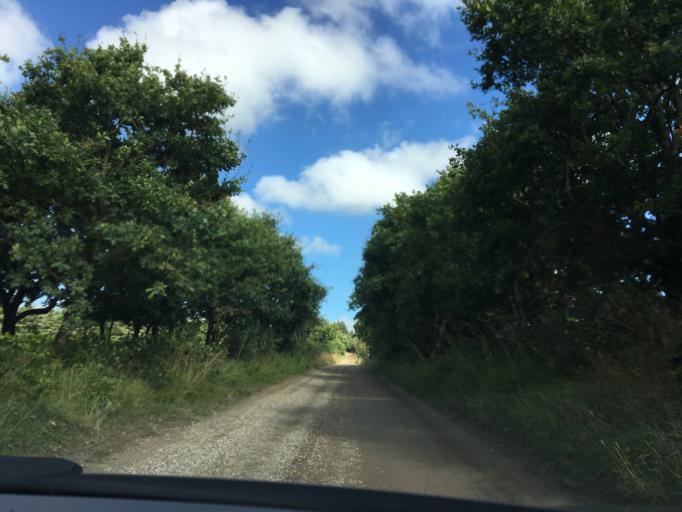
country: DK
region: South Denmark
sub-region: Varde Kommune
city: Oksbol
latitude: 55.7385
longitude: 8.2329
